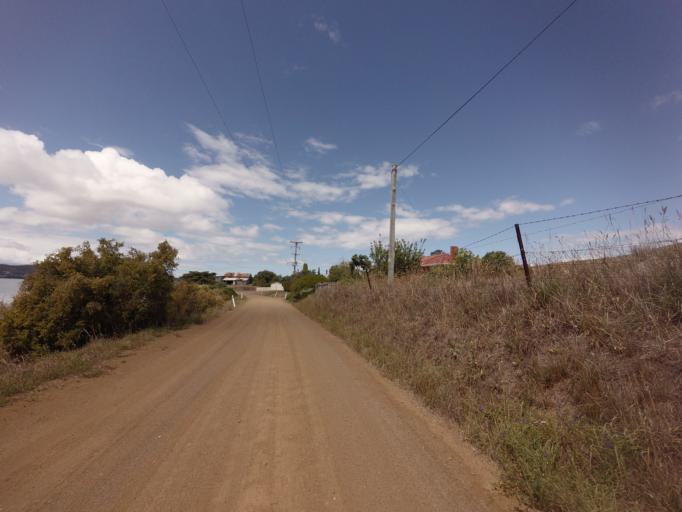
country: AU
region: Tasmania
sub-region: Clarence
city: Rokeby
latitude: -42.9157
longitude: 147.4337
